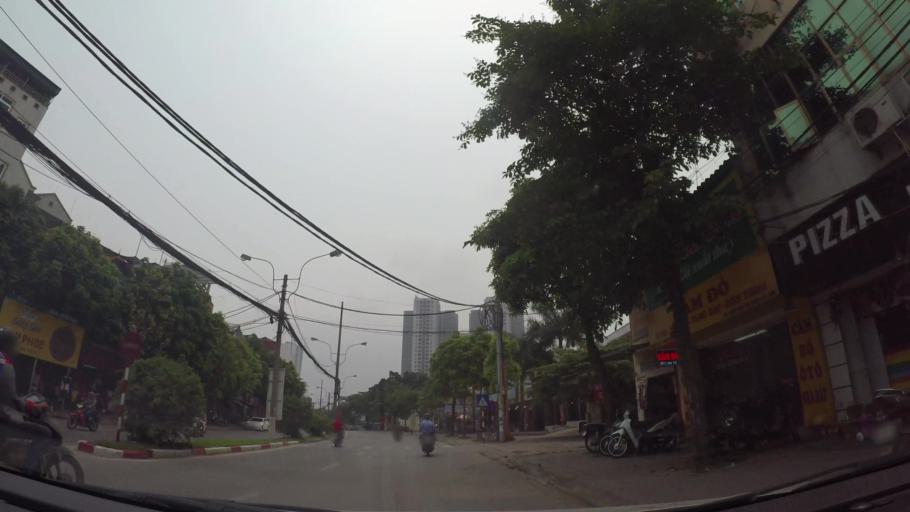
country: VN
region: Ha Noi
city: Ha Dong
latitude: 20.9791
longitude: 105.7728
